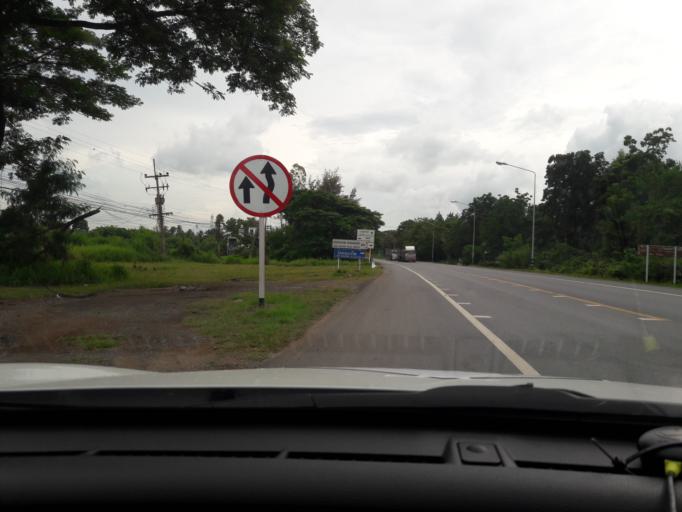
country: TH
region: Nakhon Sawan
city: Tak Fa
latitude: 15.3575
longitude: 100.5026
